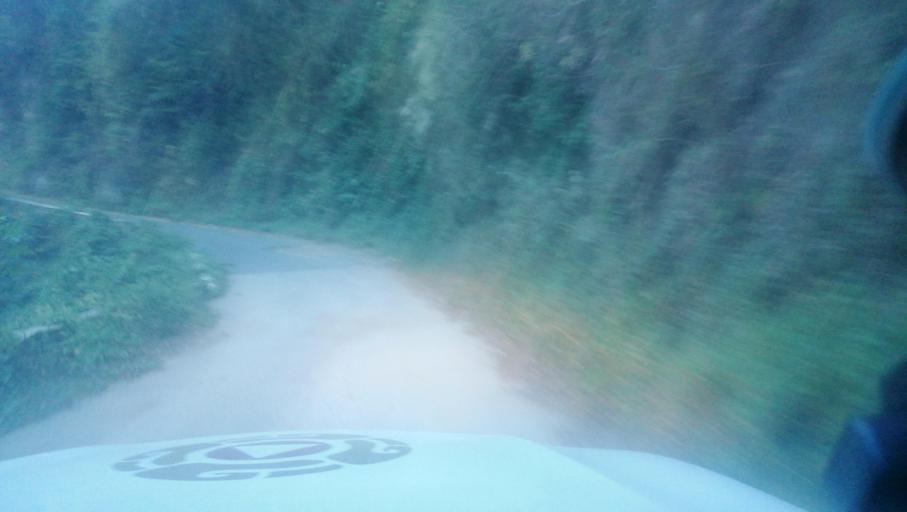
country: MX
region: Chiapas
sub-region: Cacahoatan
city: Benito Juarez
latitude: 15.1287
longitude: -92.2083
